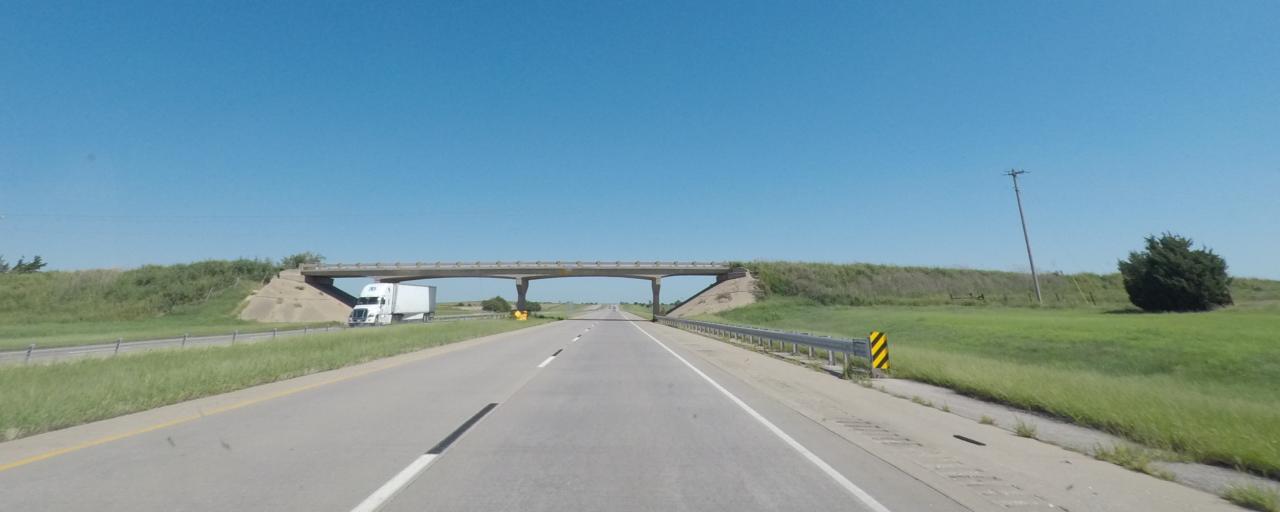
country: US
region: Oklahoma
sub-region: Kay County
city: Tonkawa
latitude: 36.5637
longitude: -97.3455
